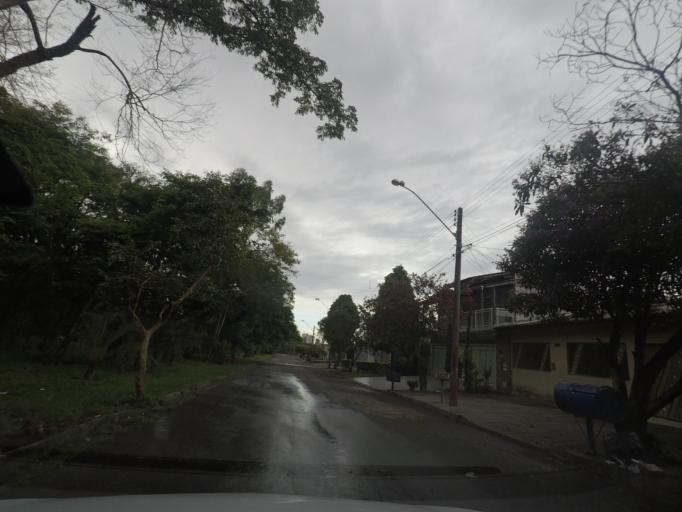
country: BR
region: Goias
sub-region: Goiania
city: Goiania
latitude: -16.7266
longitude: -49.2428
